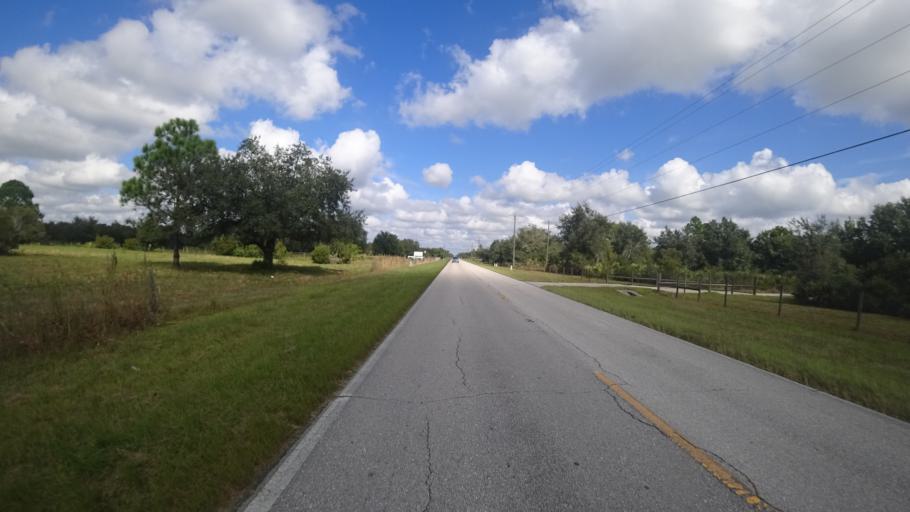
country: US
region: Florida
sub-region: Sarasota County
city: Lake Sarasota
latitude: 27.3991
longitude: -82.2711
